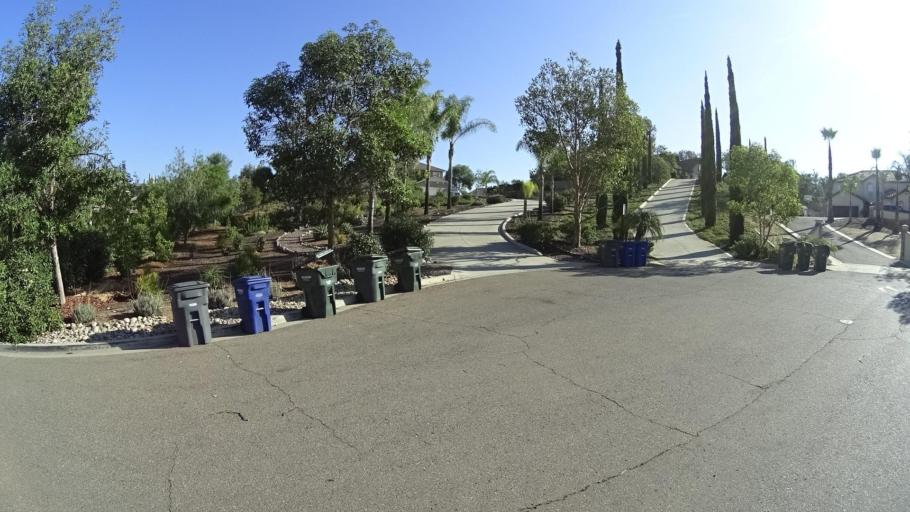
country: US
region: California
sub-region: San Diego County
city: Escondido
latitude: 33.0868
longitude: -117.0803
